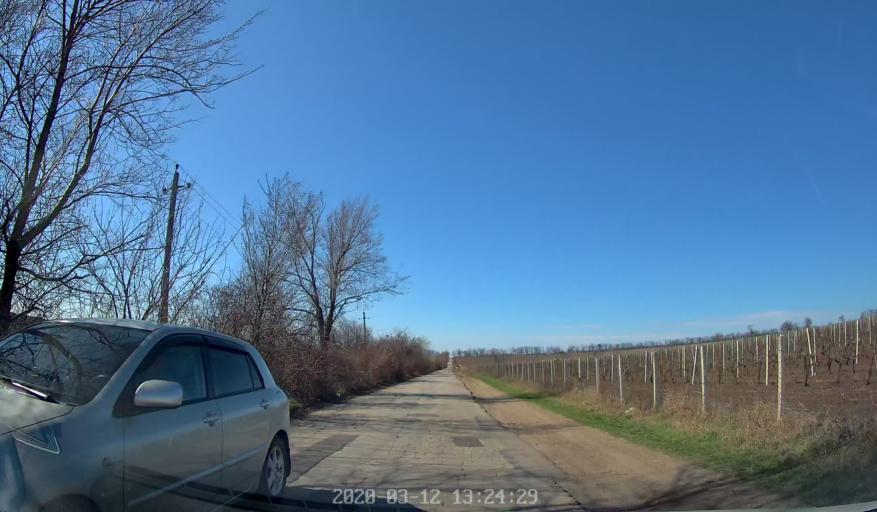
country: MD
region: Laloveni
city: Ialoveni
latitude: 46.9402
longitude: 28.8292
